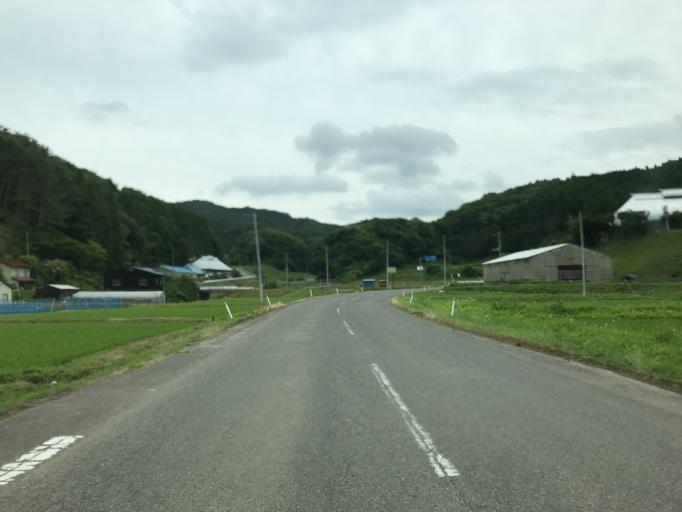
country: JP
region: Fukushima
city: Funehikimachi-funehiki
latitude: 37.3969
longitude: 140.6653
